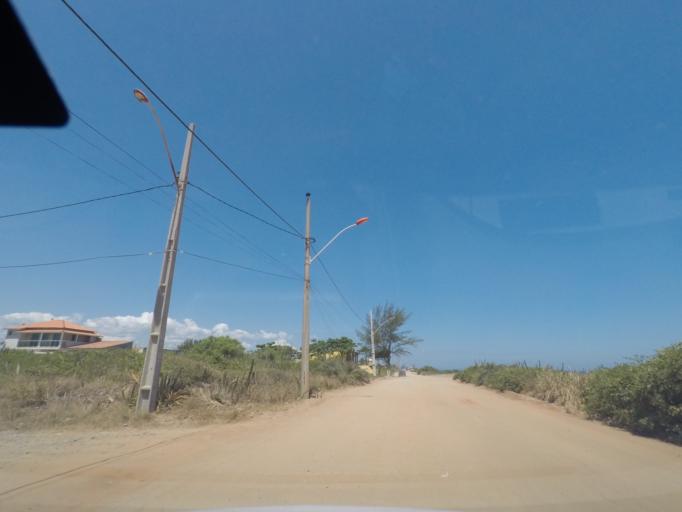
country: BR
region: Rio de Janeiro
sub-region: Marica
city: Marica
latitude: -22.9740
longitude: -42.9253
